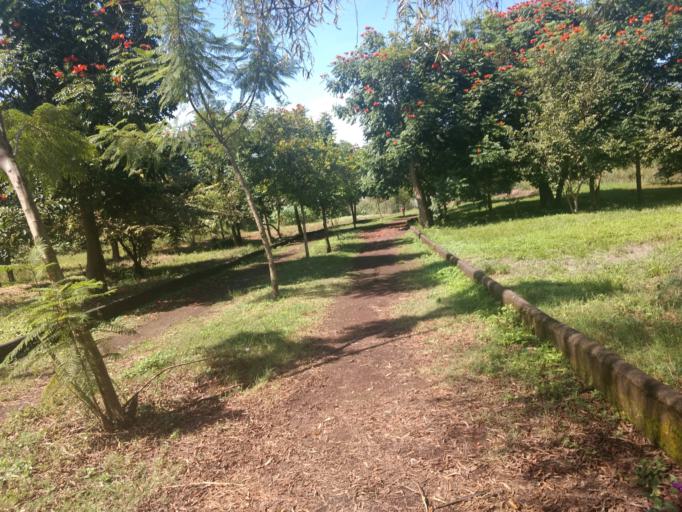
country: MX
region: Nayarit
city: Tepic
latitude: 21.4851
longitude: -104.8579
